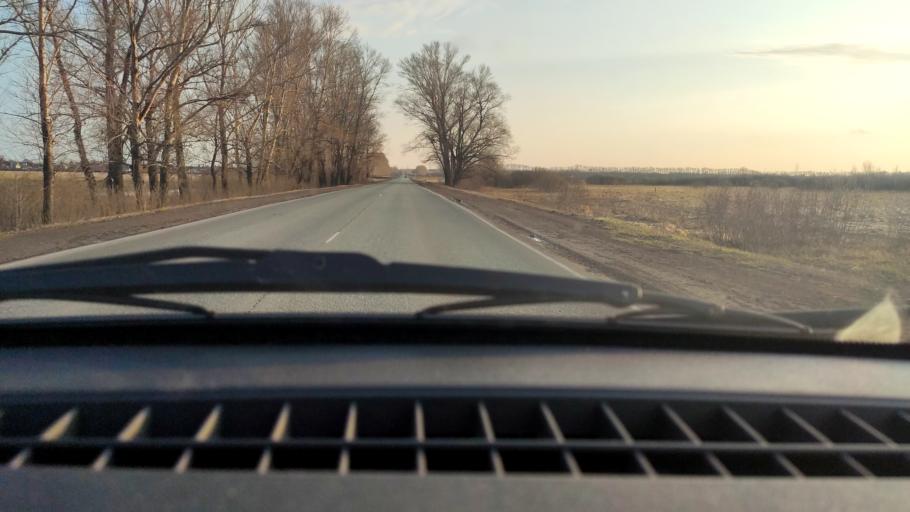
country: RU
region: Bashkortostan
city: Chishmy
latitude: 54.4040
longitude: 55.2166
